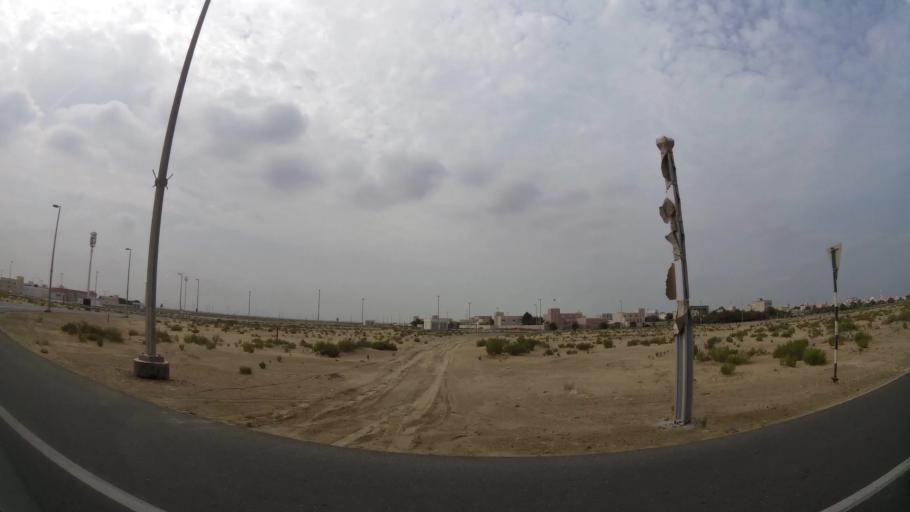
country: AE
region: Abu Dhabi
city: Abu Dhabi
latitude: 24.6370
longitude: 54.6788
